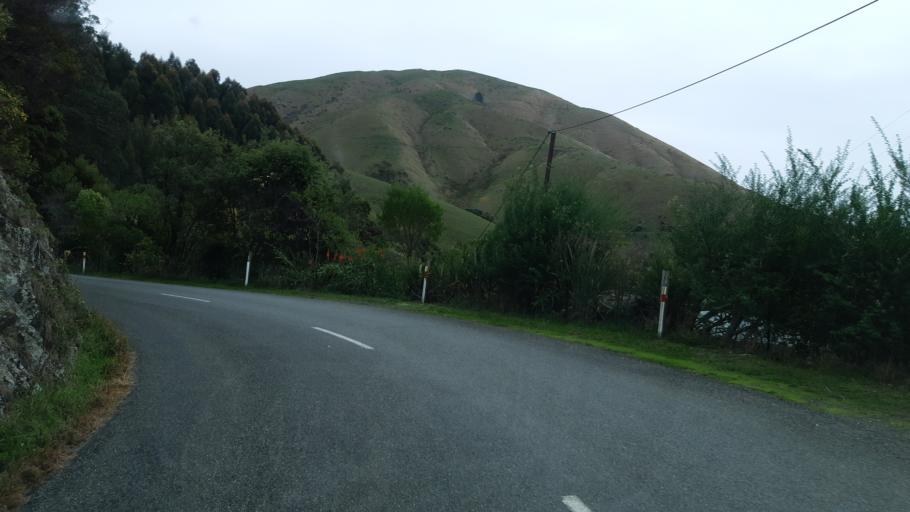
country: NZ
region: Nelson
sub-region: Nelson City
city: Nelson
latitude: -41.1641
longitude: 173.4146
